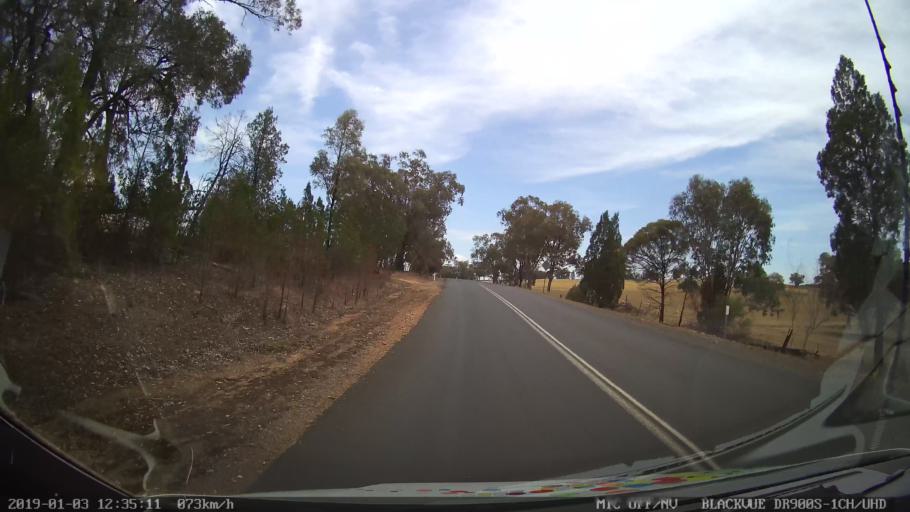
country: AU
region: New South Wales
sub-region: Weddin
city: Grenfell
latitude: -33.8693
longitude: 148.1691
